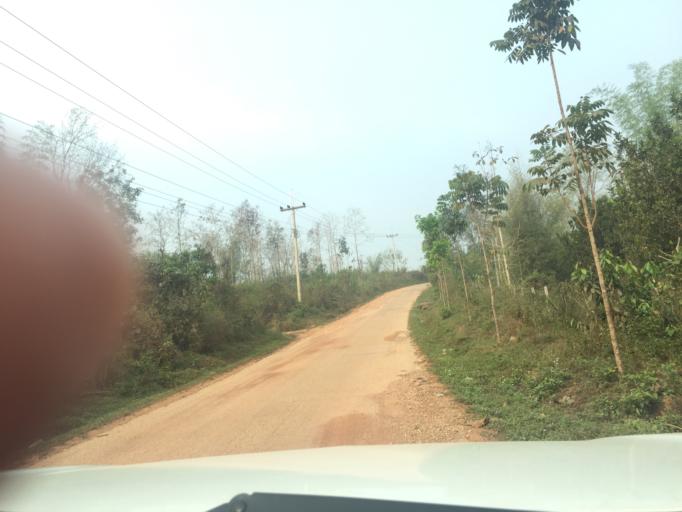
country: LA
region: Xiagnabouli
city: Sainyabuli
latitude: 19.2606
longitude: 101.6808
